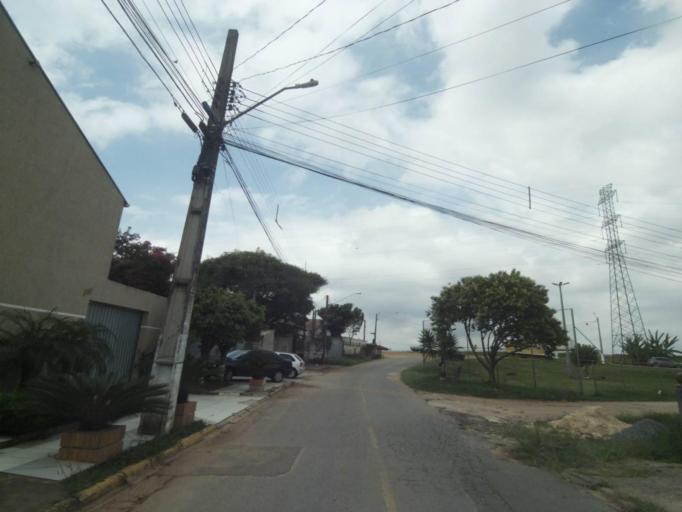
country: BR
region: Parana
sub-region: Curitiba
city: Curitiba
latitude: -25.4822
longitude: -49.3498
